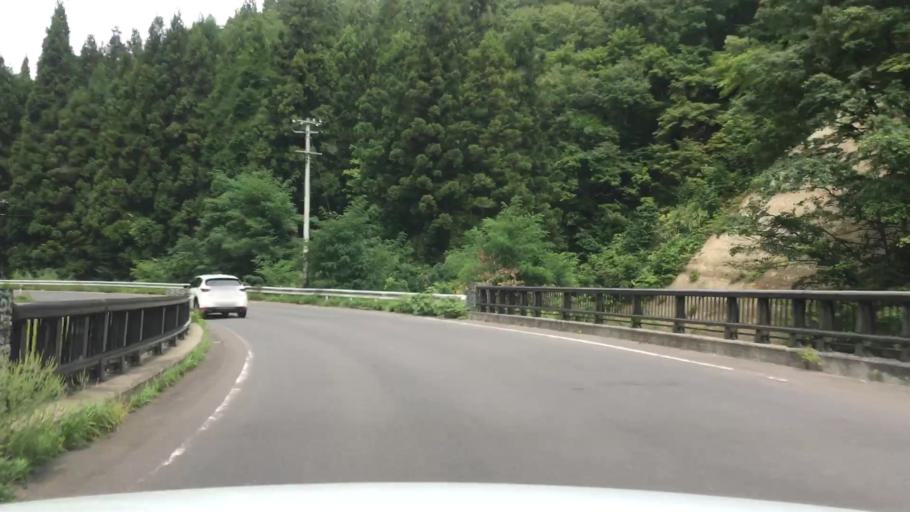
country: JP
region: Aomori
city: Shimokizukuri
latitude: 40.7355
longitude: 140.2502
